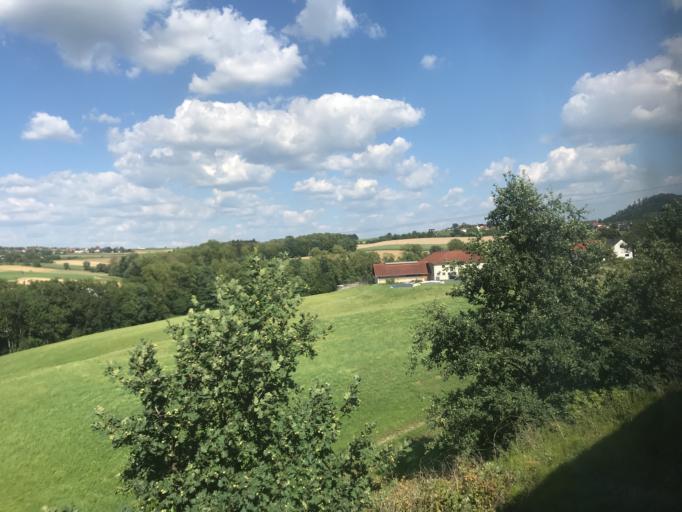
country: AT
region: Upper Austria
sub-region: Politischer Bezirk Urfahr-Umgebung
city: Engerwitzdorf
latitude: 48.3245
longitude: 14.5002
